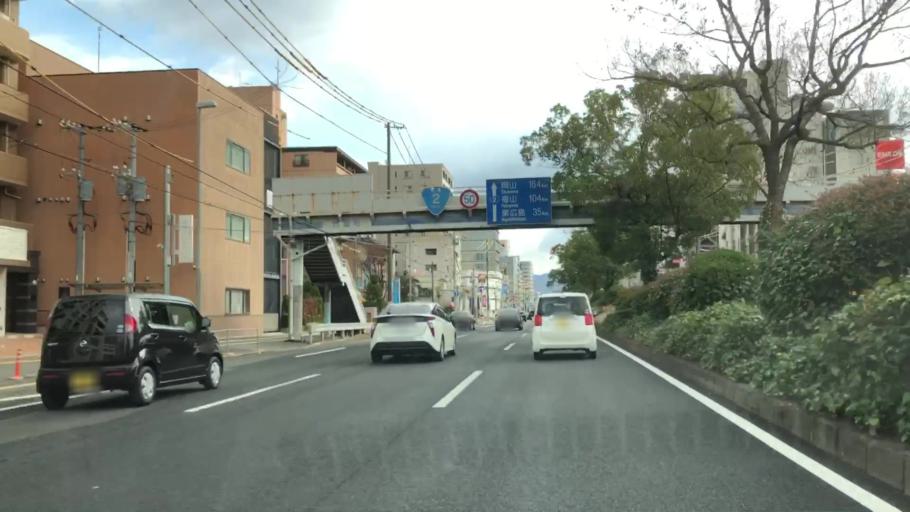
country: JP
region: Hiroshima
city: Hiroshima-shi
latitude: 34.3833
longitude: 132.4596
